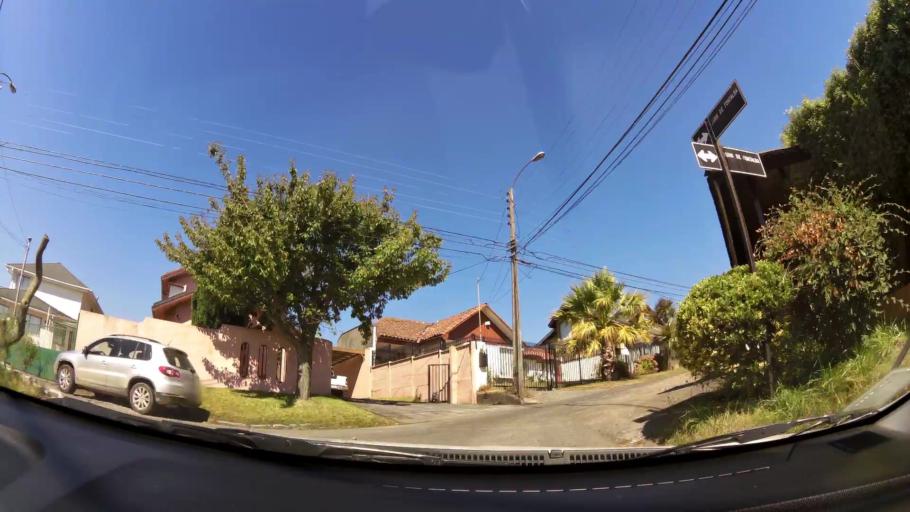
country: CL
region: Biobio
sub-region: Provincia de Concepcion
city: Concepcion
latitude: -36.7916
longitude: -73.0537
